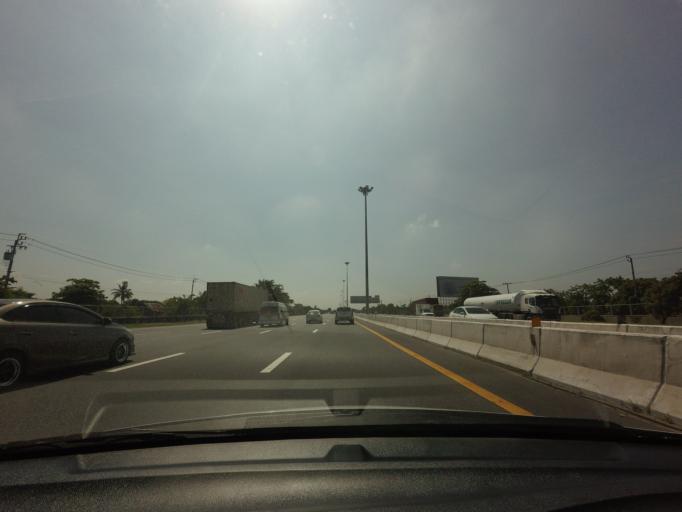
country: TH
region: Samut Prakan
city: Ban Khlong Bang Sao Thong
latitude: 13.6927
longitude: 100.8287
